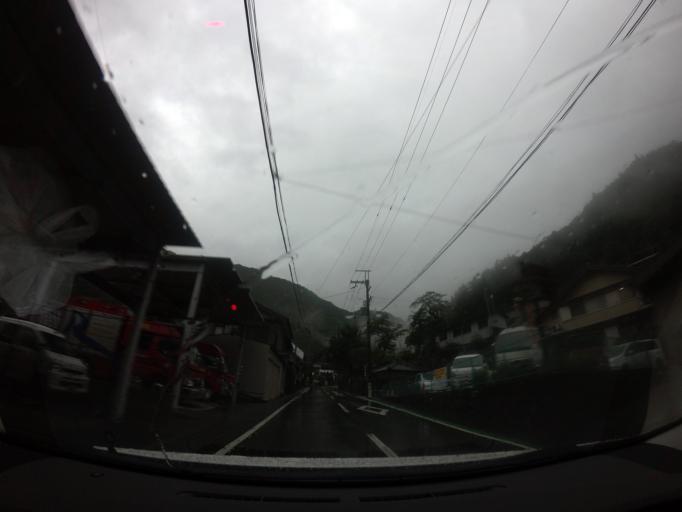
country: JP
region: Wakayama
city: Shingu
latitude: 33.9490
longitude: 135.8029
